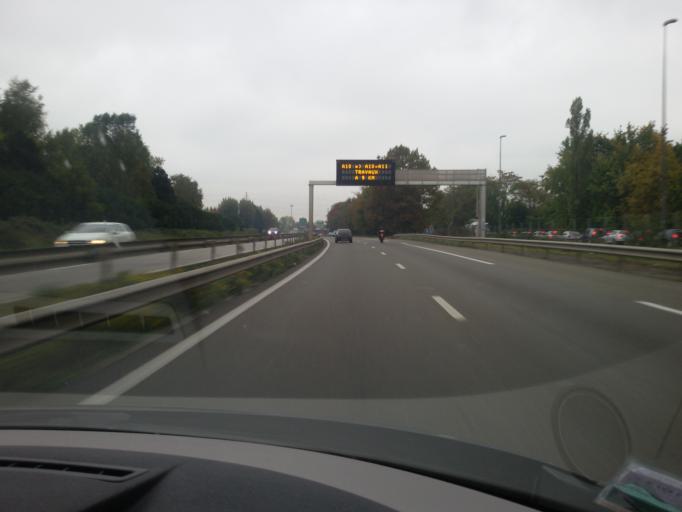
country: FR
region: Ile-de-France
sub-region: Departement de l'Essonne
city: Orsay
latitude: 48.6816
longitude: 2.1901
